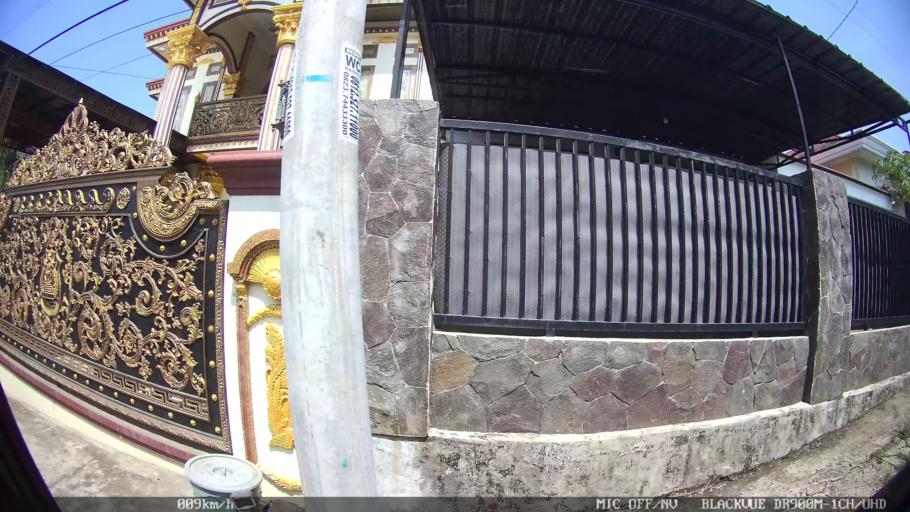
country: ID
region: Lampung
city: Kedaton
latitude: -5.3623
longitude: 105.2544
